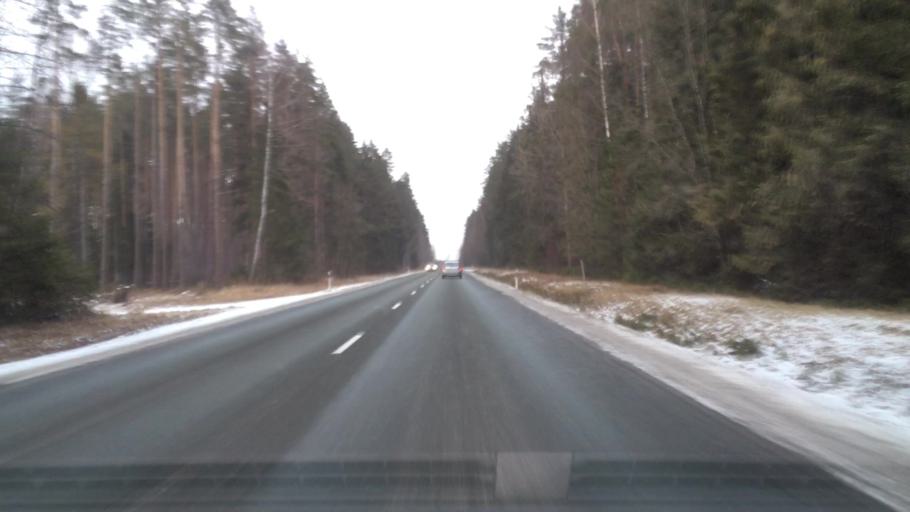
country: LV
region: Valmieras Rajons
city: Valmiera
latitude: 57.5022
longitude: 25.4192
